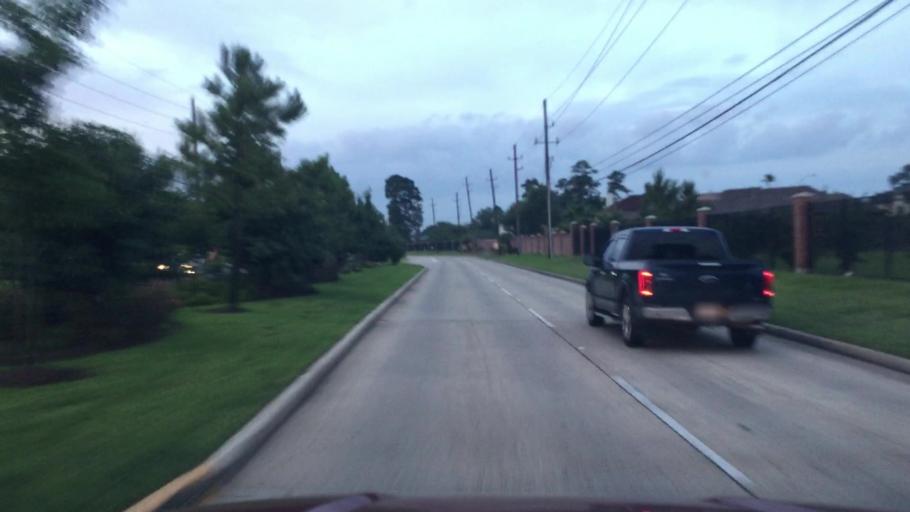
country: US
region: Texas
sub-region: Harris County
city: Tomball
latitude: 30.0357
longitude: -95.5359
